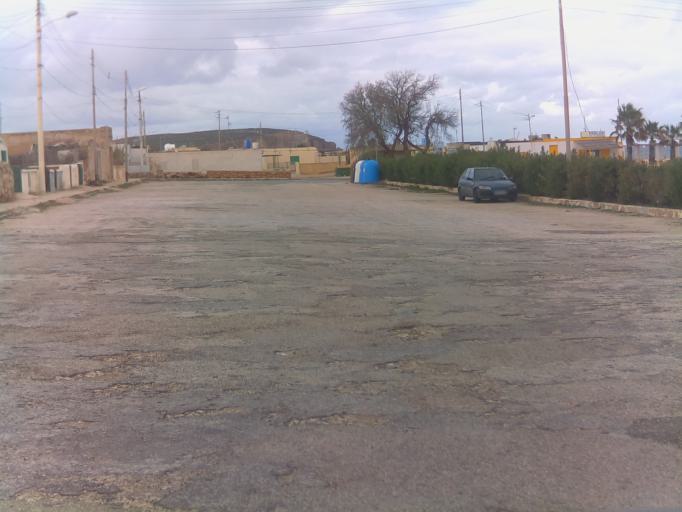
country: MT
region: Il-Mellieha
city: Mellieha
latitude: 35.9895
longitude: 14.3553
